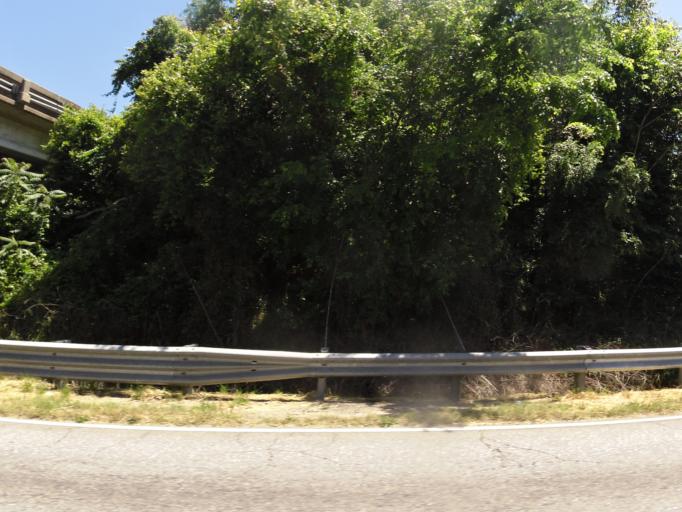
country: US
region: South Carolina
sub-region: Aiken County
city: North Augusta
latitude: 33.4832
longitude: -81.9482
